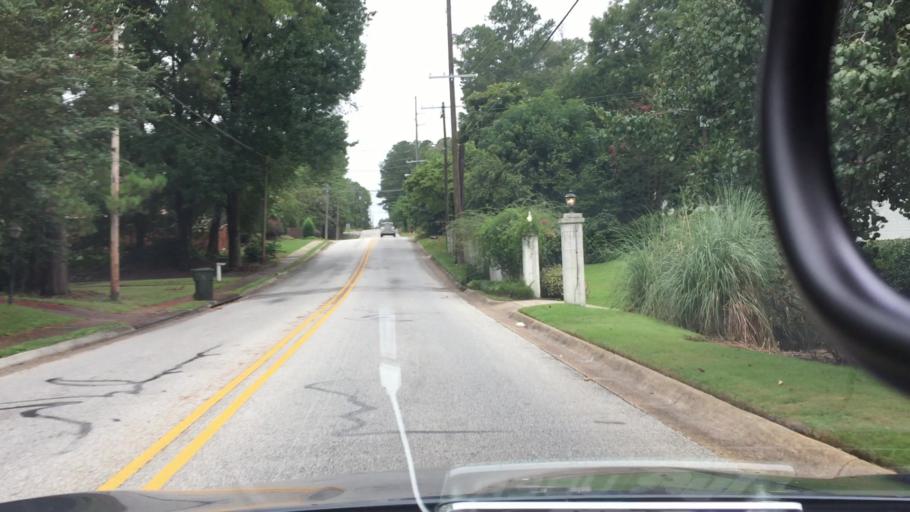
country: US
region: Alabama
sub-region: Lee County
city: Auburn
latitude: 32.6141
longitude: -85.4840
